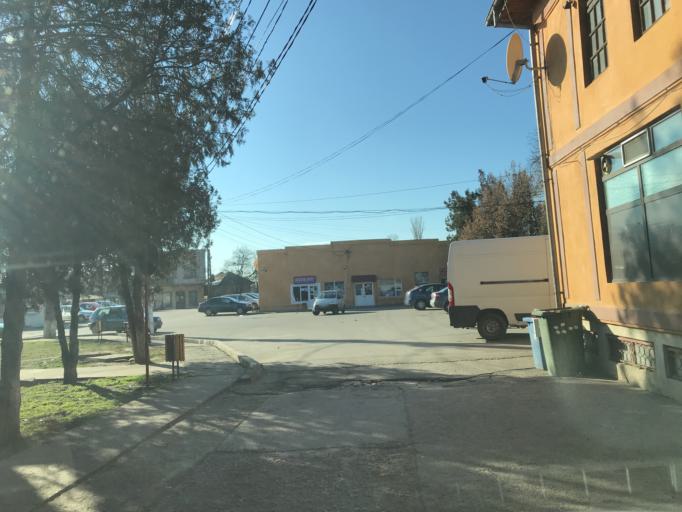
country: RO
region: Olt
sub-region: Comuna Piatra Olt
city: Piatra Olt
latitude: 44.3680
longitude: 24.2558
